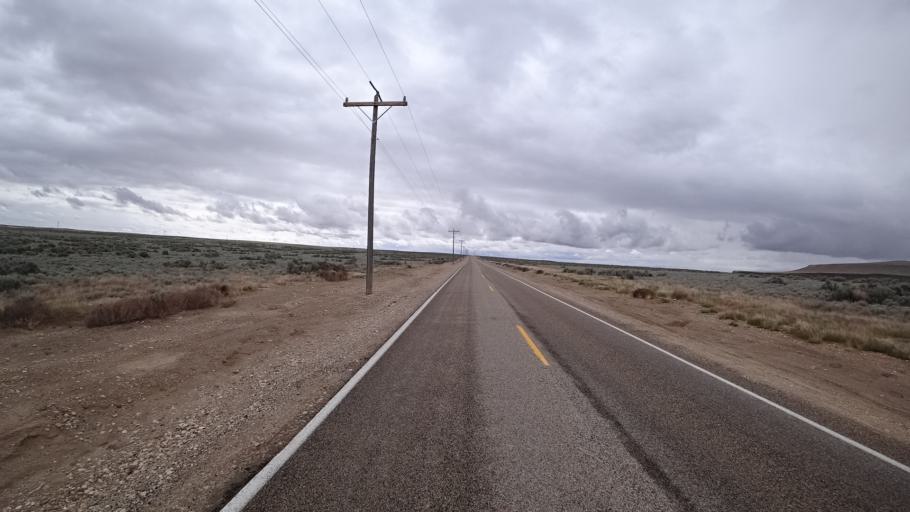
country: US
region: Idaho
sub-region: Owyhee County
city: Murphy
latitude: 43.2571
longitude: -116.3775
